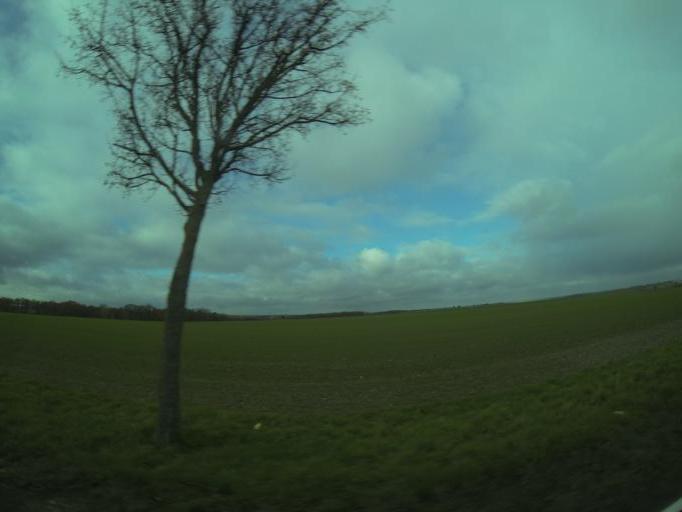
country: DE
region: Thuringia
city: Schmolln
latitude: 50.8726
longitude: 12.3651
